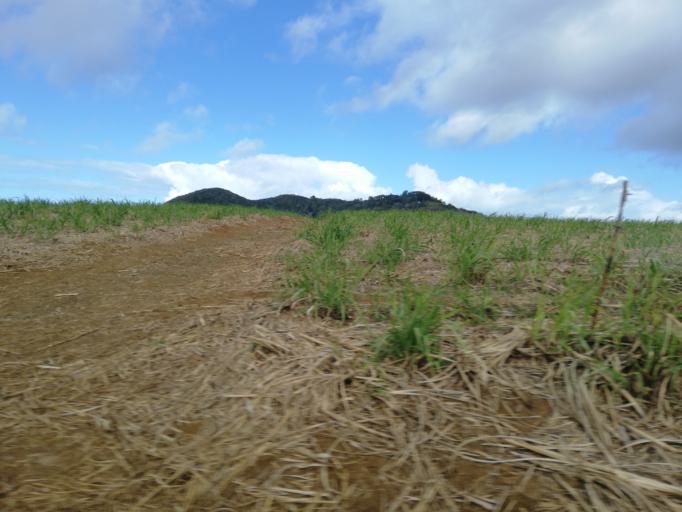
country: MU
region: Flacq
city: Grande Riviere Sud Est
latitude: -20.2828
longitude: 57.7559
